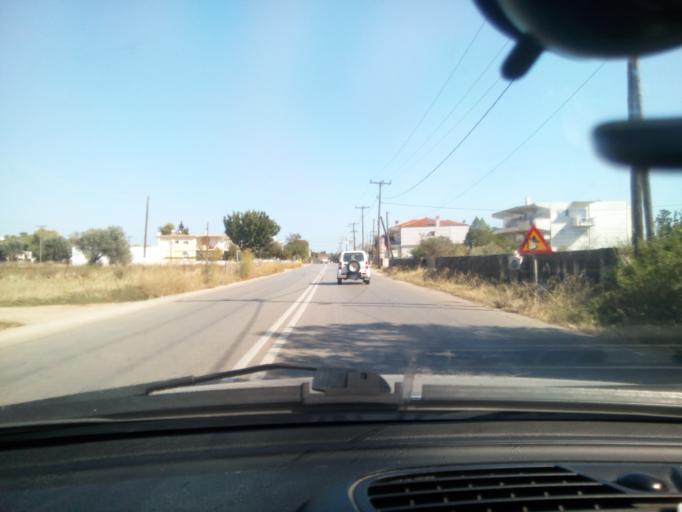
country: GR
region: Central Greece
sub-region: Nomos Evvoias
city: Malakonta
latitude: 38.4020
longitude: 23.7546
